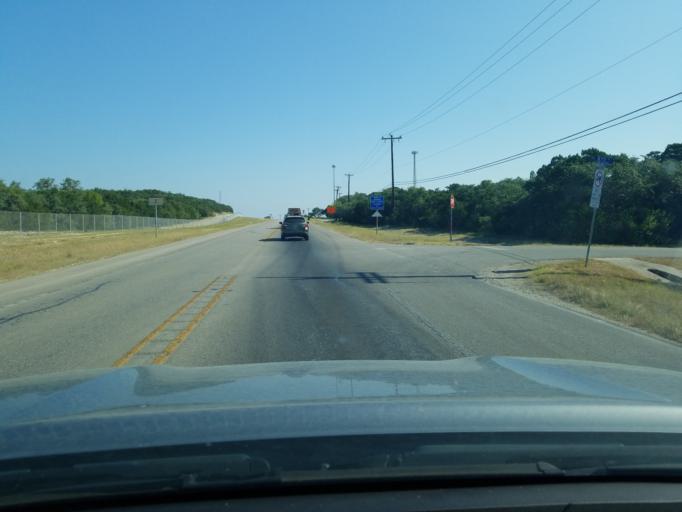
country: US
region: Texas
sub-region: Bexar County
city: Timberwood Park
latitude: 29.6971
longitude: -98.5213
